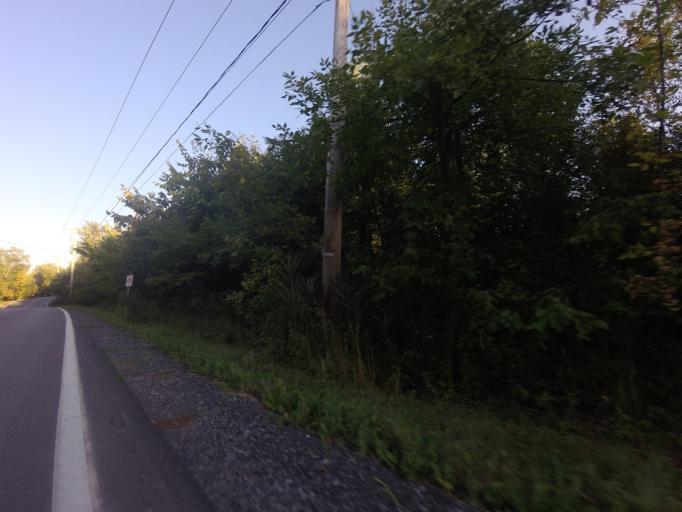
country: CA
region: Quebec
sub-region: Monteregie
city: Hudson
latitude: 45.4711
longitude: -74.1762
